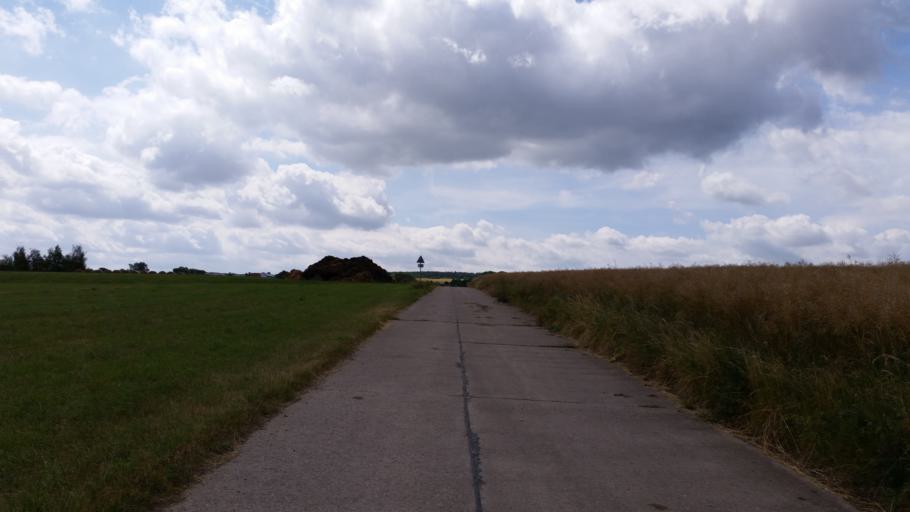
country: DE
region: Thuringia
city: Mellingen
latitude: 50.9194
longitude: 11.3935
